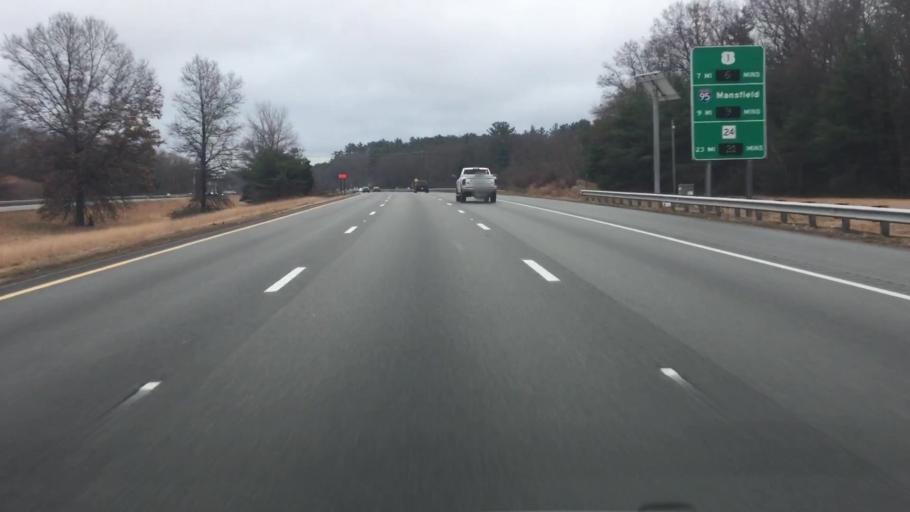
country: US
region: Massachusetts
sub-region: Norfolk County
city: Franklin
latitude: 42.0831
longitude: -71.4230
